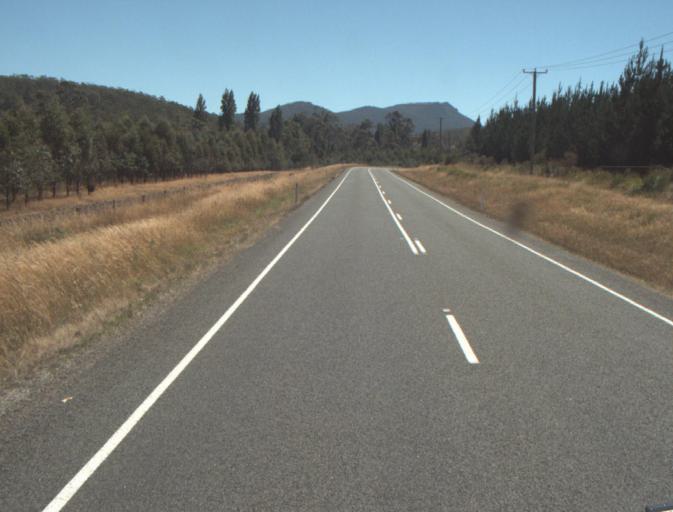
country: AU
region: Tasmania
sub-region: Launceston
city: Newstead
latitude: -41.3810
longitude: 147.3117
